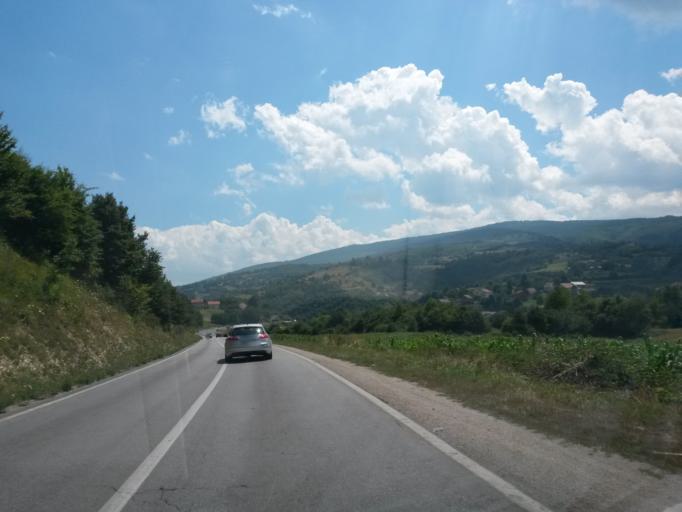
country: BA
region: Federation of Bosnia and Herzegovina
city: Turbe
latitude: 44.2381
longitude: 17.6070
